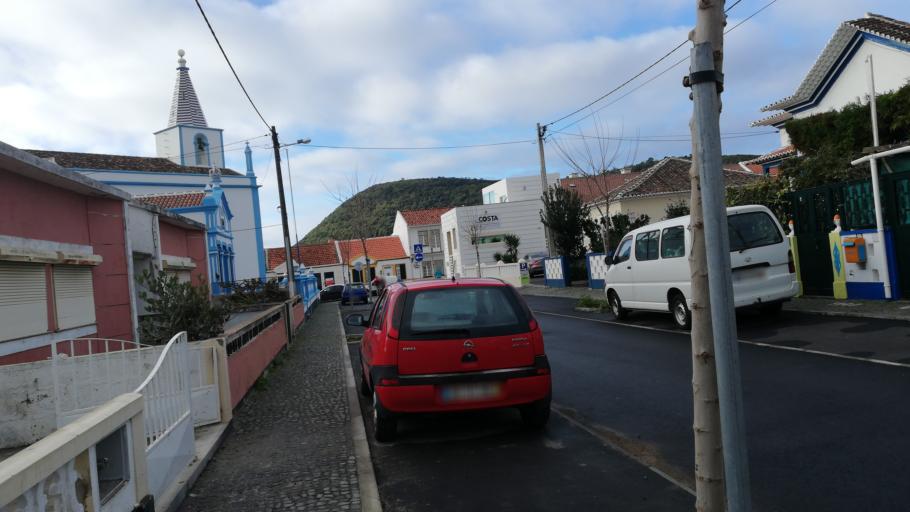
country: PT
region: Azores
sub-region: Angra do Heroismo
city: Angra do Heroismo
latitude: 38.6541
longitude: -27.2148
